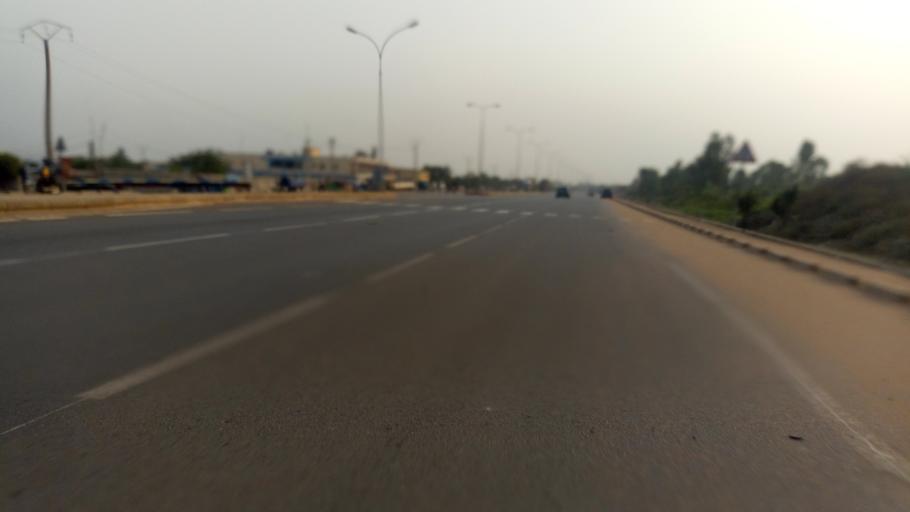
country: TG
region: Maritime
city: Lome
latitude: 6.2688
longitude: 1.2095
